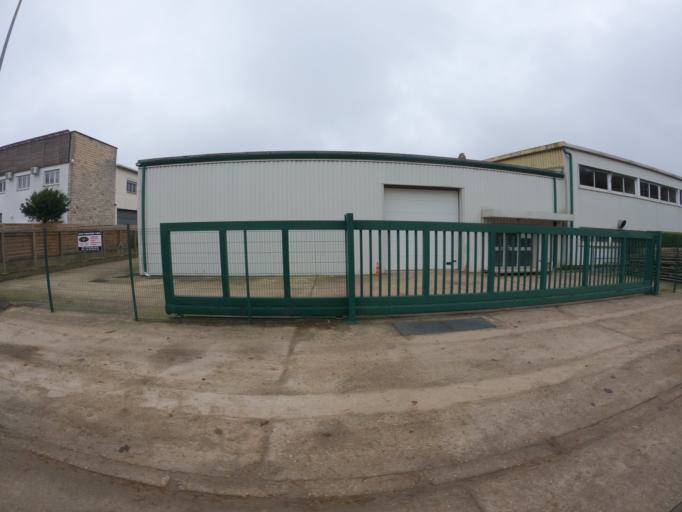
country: FR
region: Ile-de-France
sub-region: Departement du Val-de-Marne
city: Chennevieres-sur-Marne
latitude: 48.7959
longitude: 2.5417
